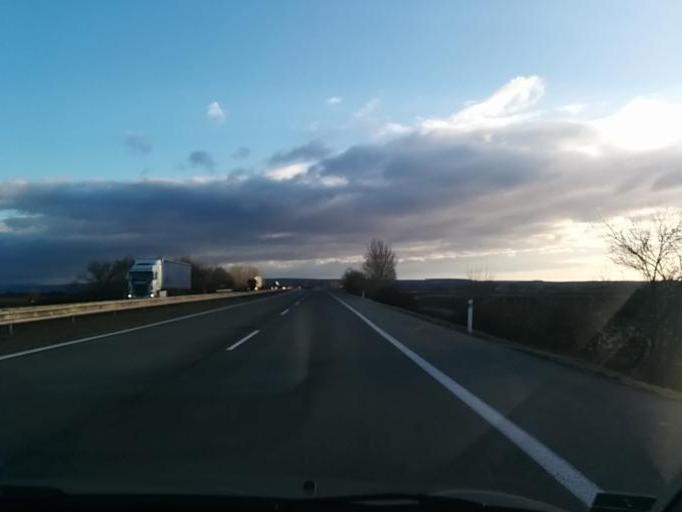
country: SK
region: Trnavsky
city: Leopoldov
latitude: 48.3702
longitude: 17.7178
